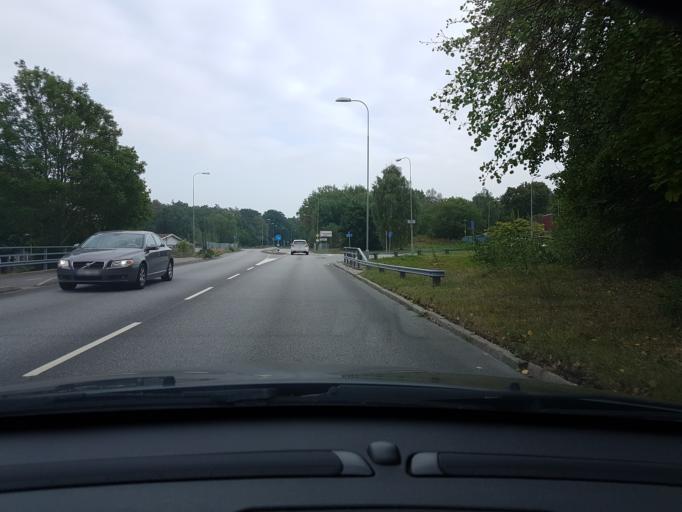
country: SE
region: Vaestra Goetaland
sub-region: Goteborg
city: Majorna
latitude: 57.6407
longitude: 11.8966
